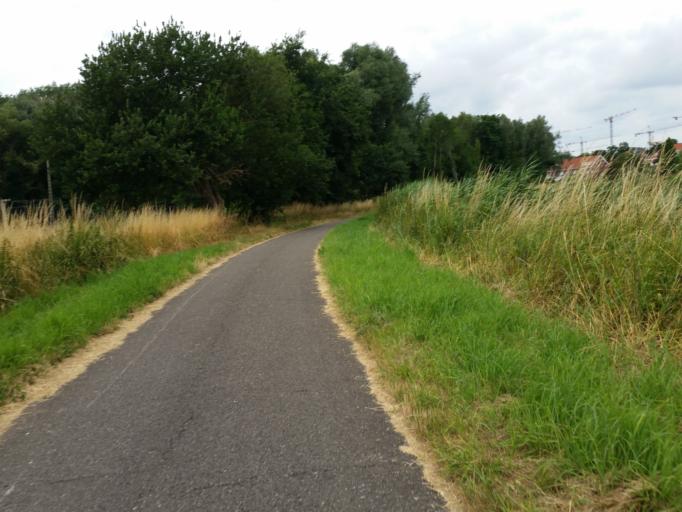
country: BE
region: Flanders
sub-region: Provincie Antwerpen
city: Mechelen
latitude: 51.0426
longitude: 4.4822
